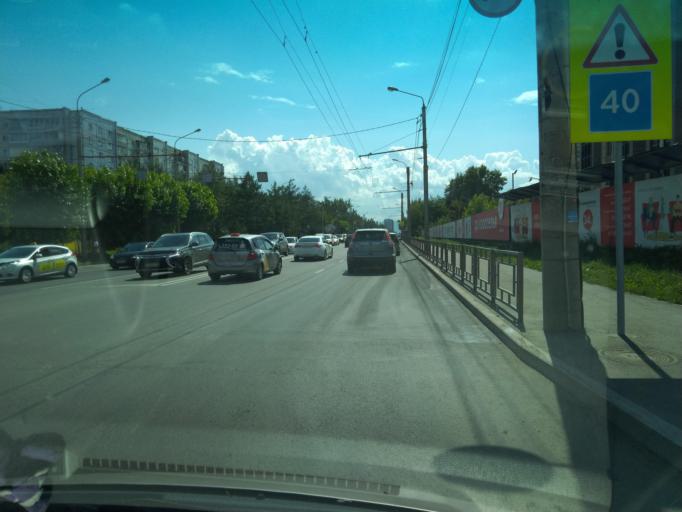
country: RU
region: Krasnoyarskiy
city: Solnechnyy
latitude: 56.0538
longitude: 92.9412
